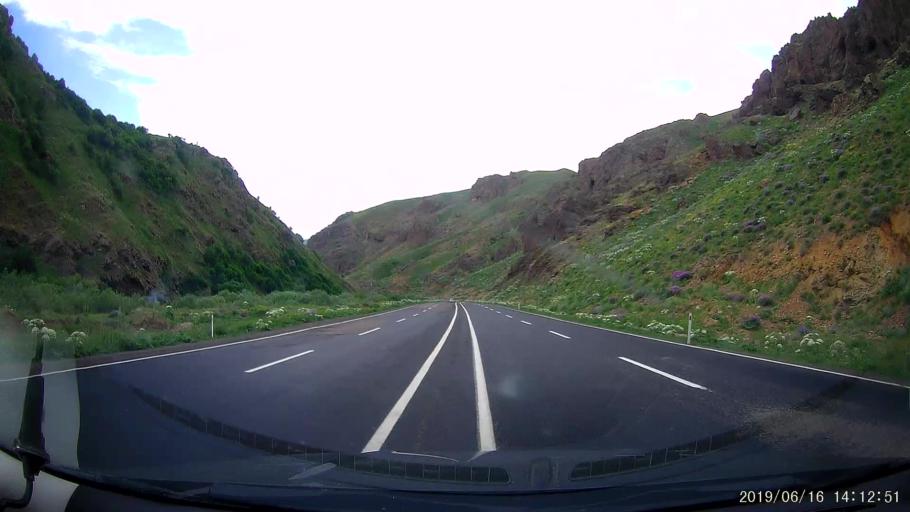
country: TR
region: Agri
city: Tahir
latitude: 39.7993
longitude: 42.5290
